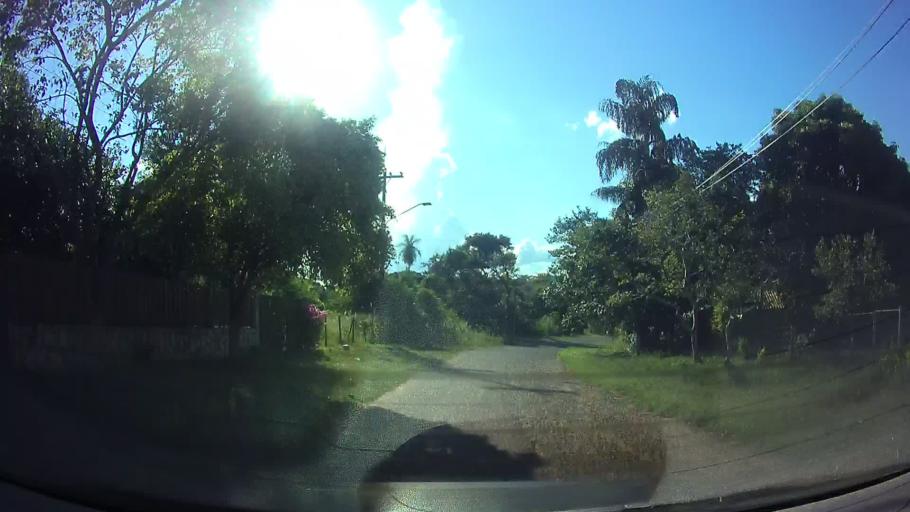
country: PY
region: Central
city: Aregua
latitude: -25.3340
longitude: -57.3806
